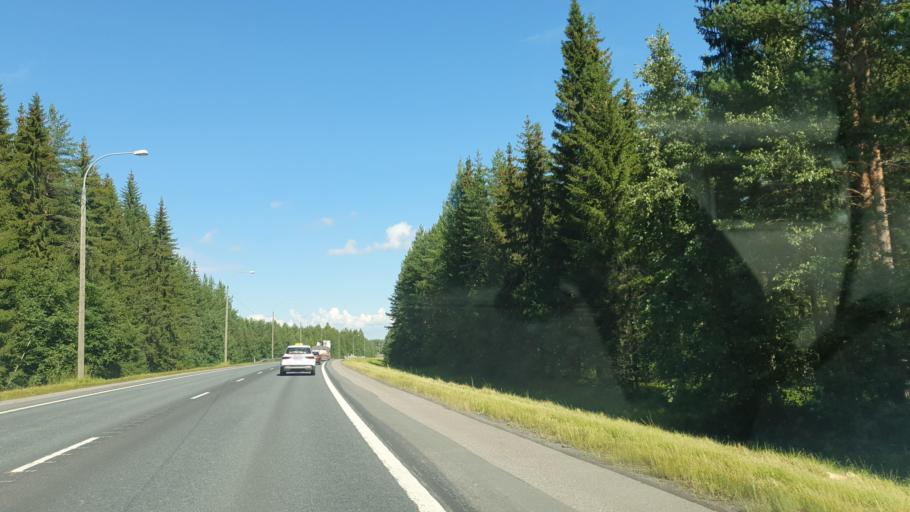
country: FI
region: Northern Savo
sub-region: Ylae-Savo
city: Iisalmi
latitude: 63.5091
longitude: 27.2569
